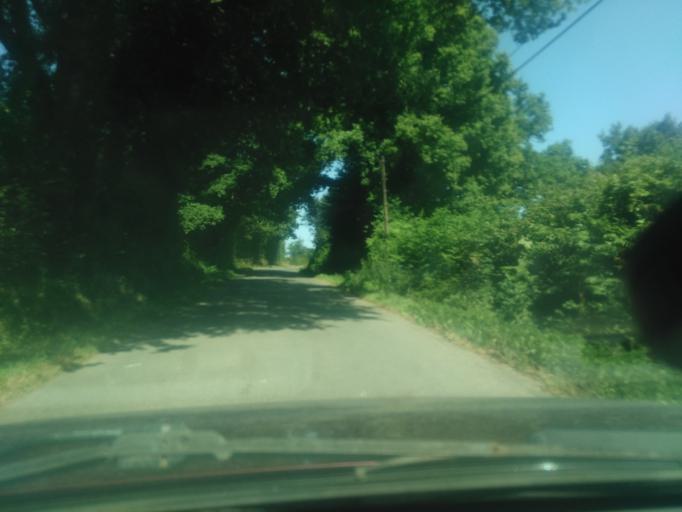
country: FR
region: Pays de la Loire
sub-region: Departement de la Vendee
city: Dompierre-sur-Yon
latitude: 46.7177
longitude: -1.3535
